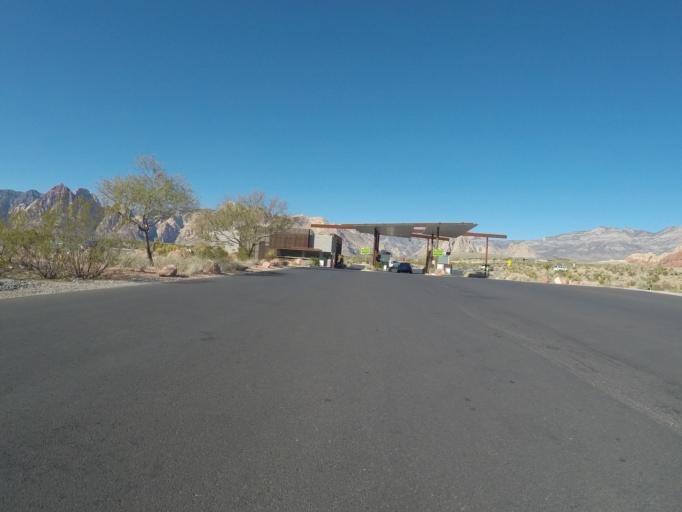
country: US
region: Nevada
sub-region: Clark County
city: Summerlin South
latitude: 36.1323
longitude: -115.4232
